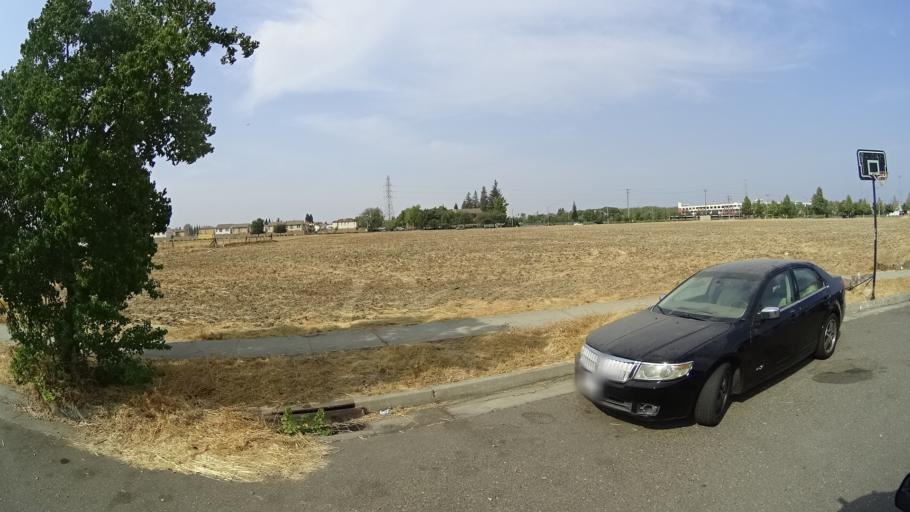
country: US
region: California
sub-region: Sacramento County
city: Laguna
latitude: 38.4490
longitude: -121.4156
